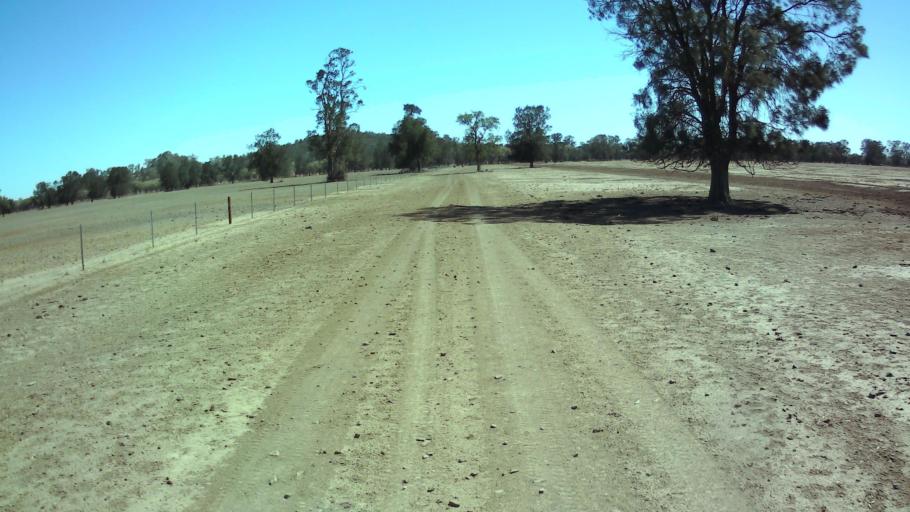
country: AU
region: New South Wales
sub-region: Bland
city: West Wyalong
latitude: -33.7441
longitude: 147.6612
